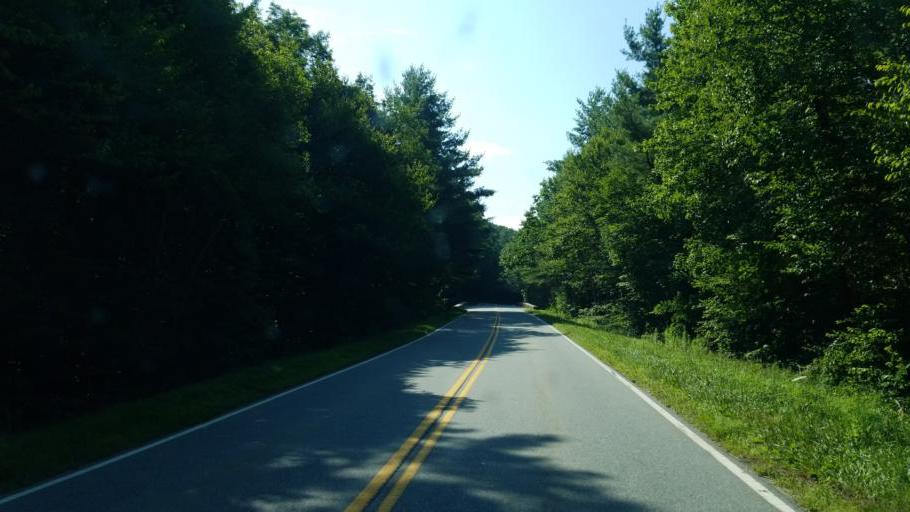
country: US
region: North Carolina
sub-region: Avery County
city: Newland
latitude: 36.0055
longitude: -81.8914
